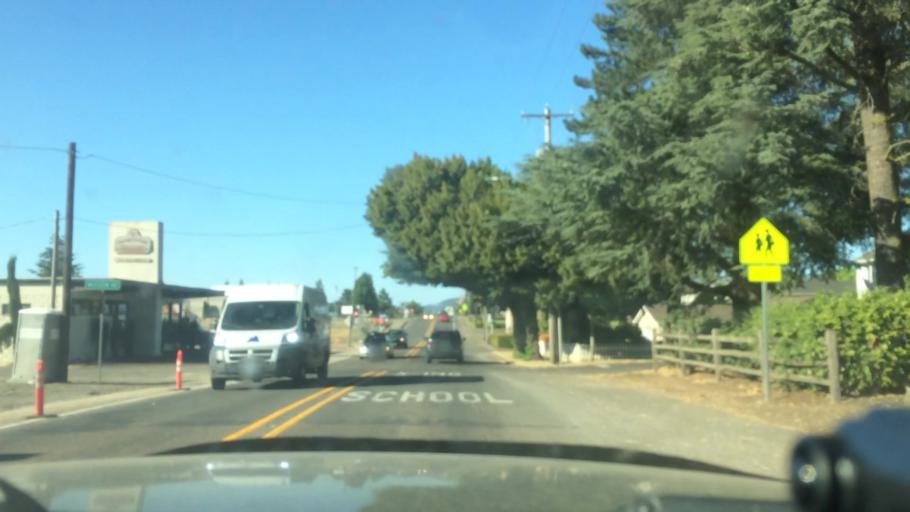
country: US
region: Oregon
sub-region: Yamhill County
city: Dundee
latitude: 45.2114
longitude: -122.9764
